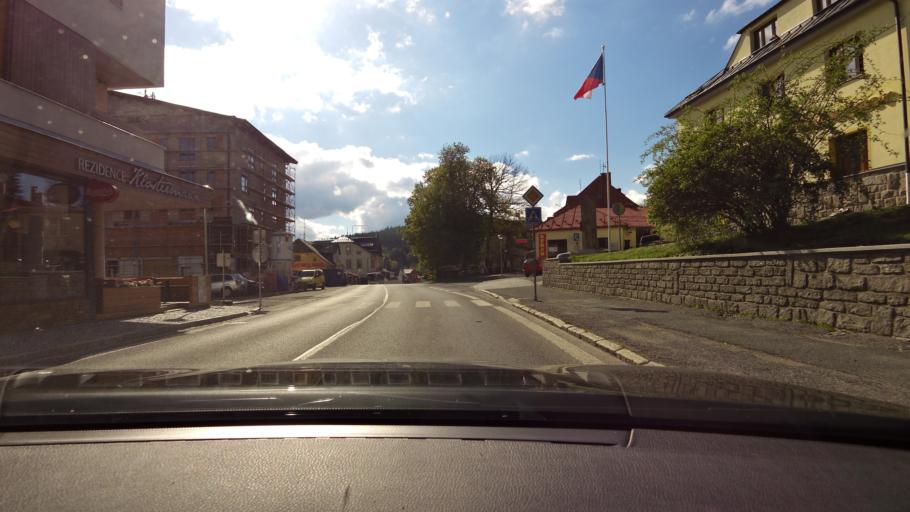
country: CZ
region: Plzensky
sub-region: Okres Klatovy
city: Zelezna Ruda
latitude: 49.1372
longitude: 13.2337
